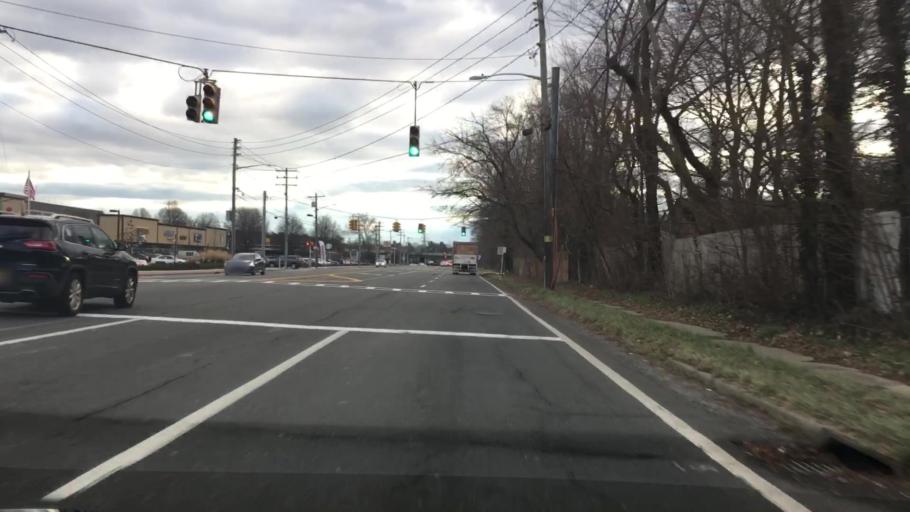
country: US
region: New York
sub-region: Suffolk County
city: Commack
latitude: 40.8087
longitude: -73.2945
